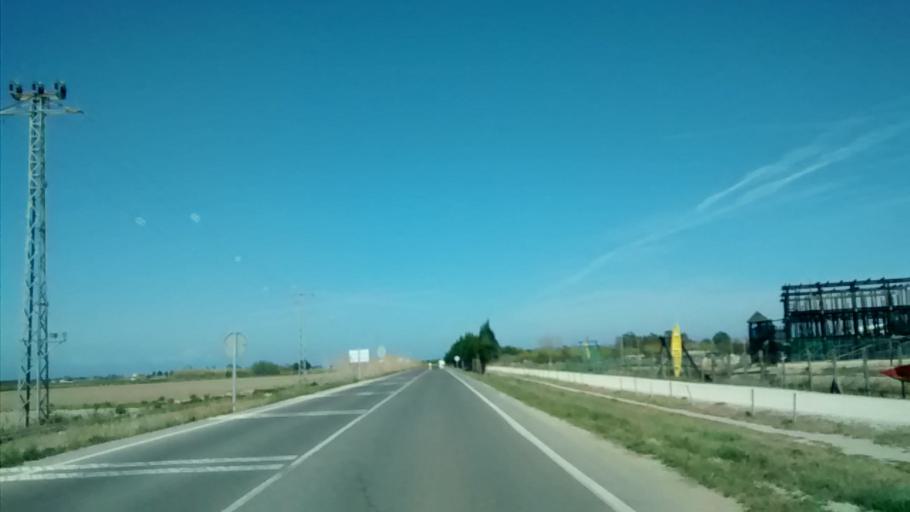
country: ES
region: Catalonia
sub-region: Provincia de Tarragona
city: Deltebre
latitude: 40.7079
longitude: 0.8124
